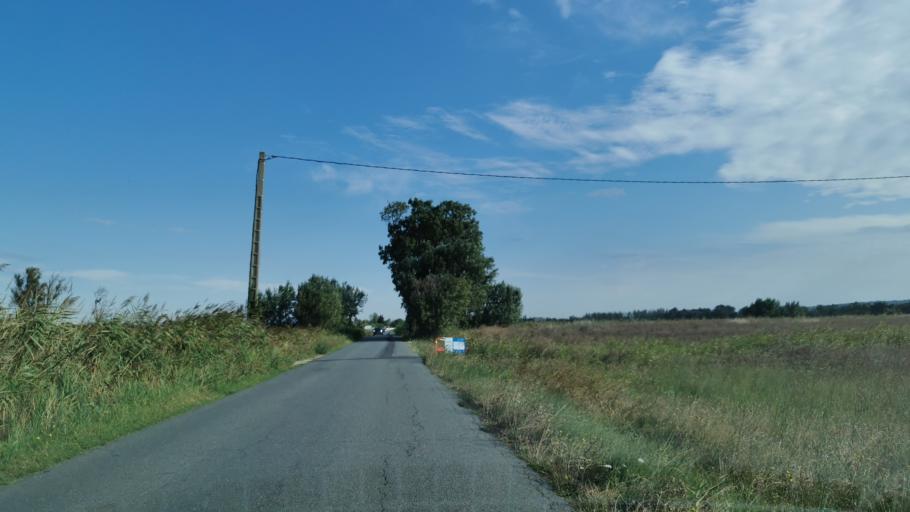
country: FR
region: Languedoc-Roussillon
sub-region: Departement de l'Aude
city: Narbonne
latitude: 43.1307
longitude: 3.0249
